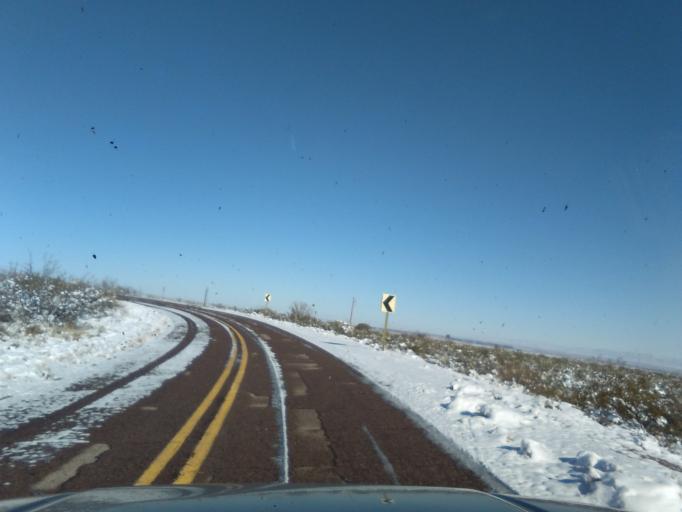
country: US
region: New Mexico
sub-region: Sierra County
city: Elephant Butte
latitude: 33.6198
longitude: -107.1377
